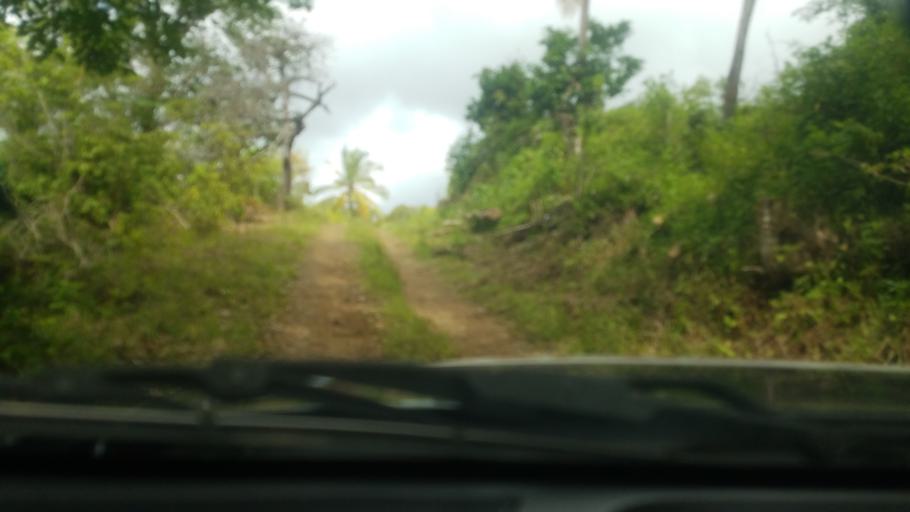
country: LC
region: Micoud Quarter
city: Micoud
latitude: 13.8059
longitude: -60.9318
